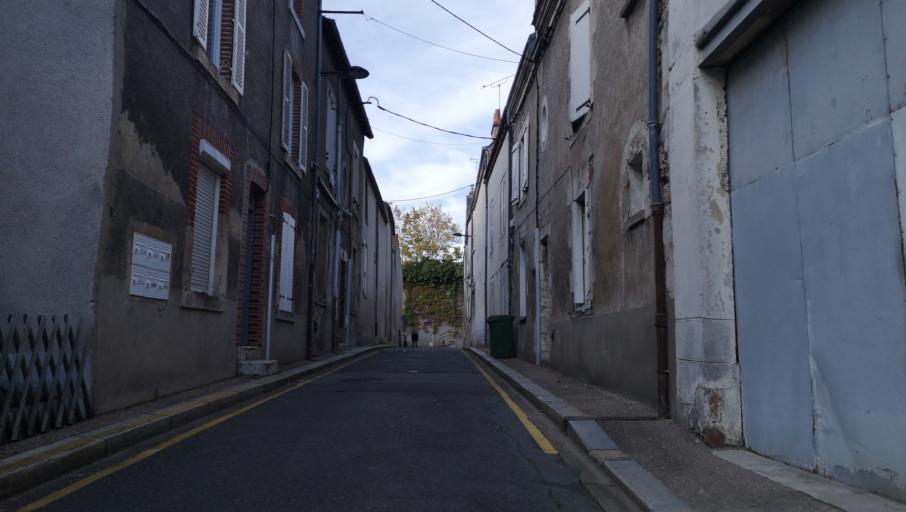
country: FR
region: Centre
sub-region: Departement du Loiret
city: Orleans
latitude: 47.8991
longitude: 1.8968
